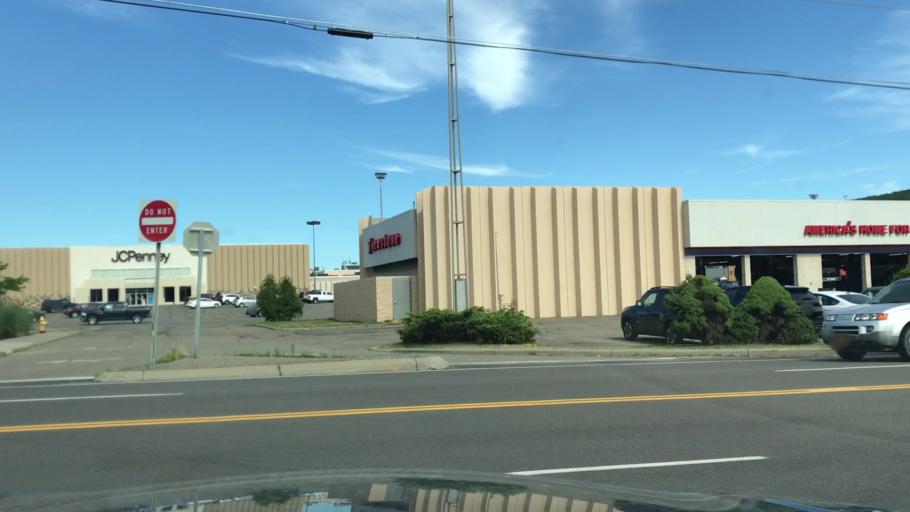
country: US
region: New York
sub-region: Chemung County
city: Horseheads
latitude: 42.1608
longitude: -76.8783
